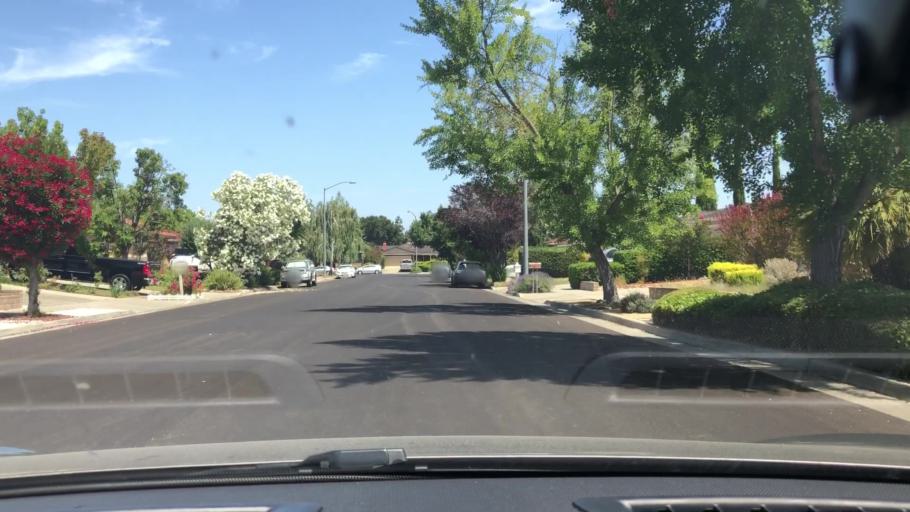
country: US
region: California
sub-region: Santa Clara County
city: Monte Sereno
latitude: 37.2639
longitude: -121.9893
